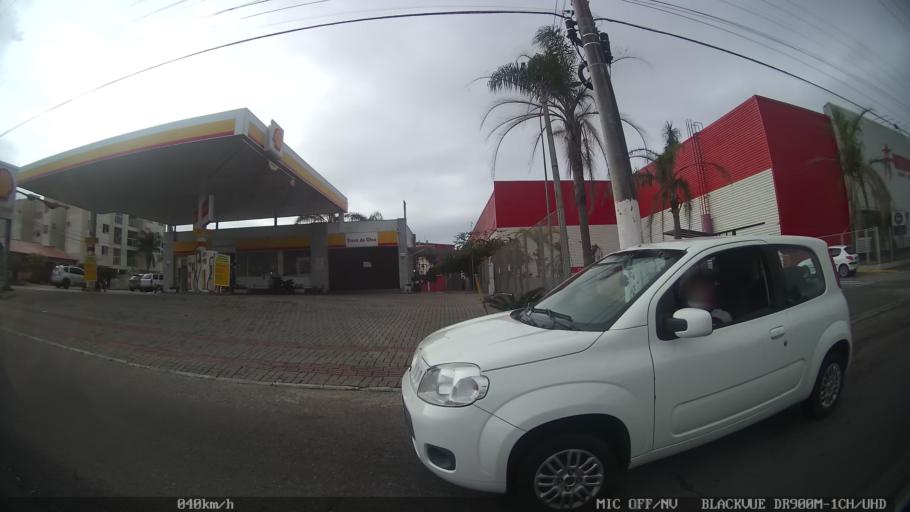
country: BR
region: Santa Catarina
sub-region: Sao Jose
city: Campinas
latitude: -27.5752
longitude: -48.6253
